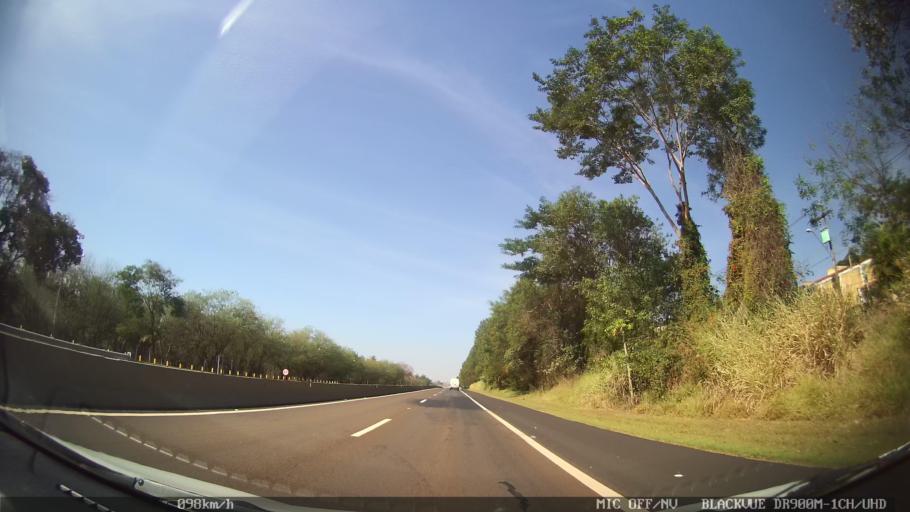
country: BR
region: Sao Paulo
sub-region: Ribeirao Preto
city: Ribeirao Preto
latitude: -21.1701
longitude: -47.8649
